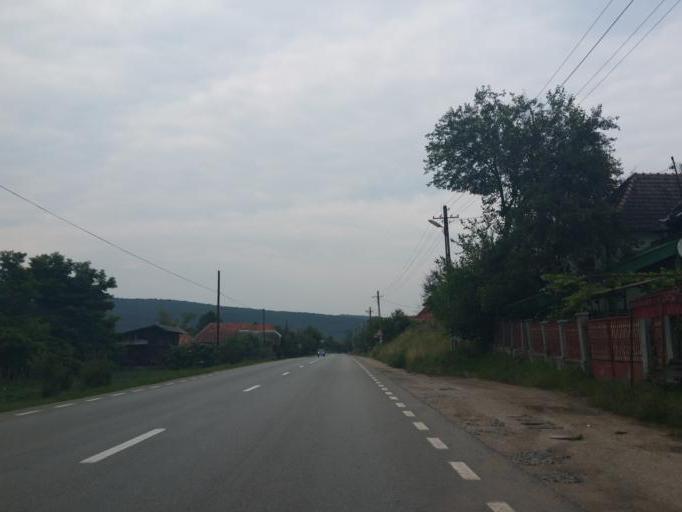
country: RO
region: Salaj
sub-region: Comuna Zimbor
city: Zimbor
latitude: 46.9815
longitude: 23.2522
